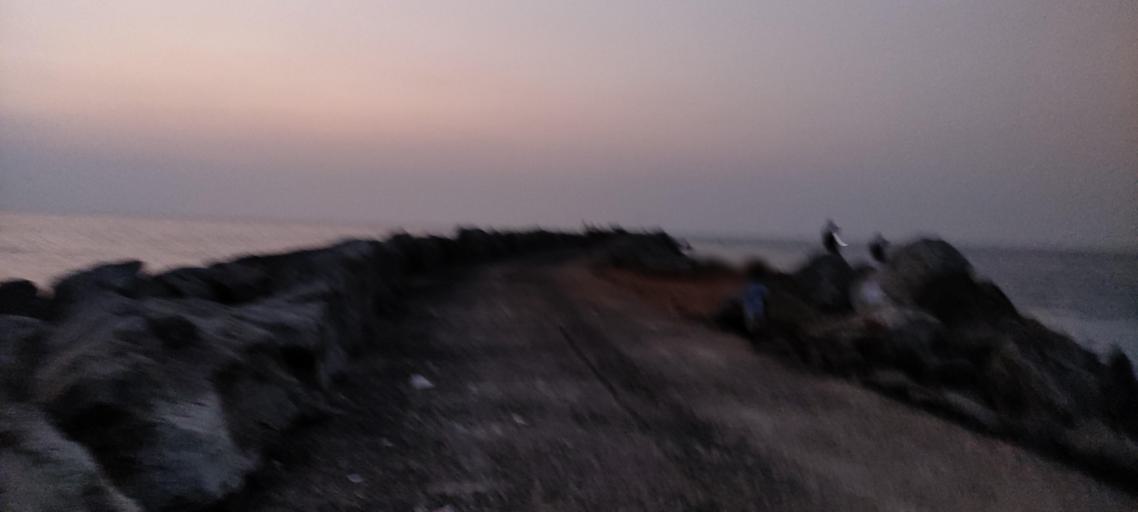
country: IN
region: Kerala
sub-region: Alappuzha
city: Kayankulam
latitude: 9.1349
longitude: 76.4604
